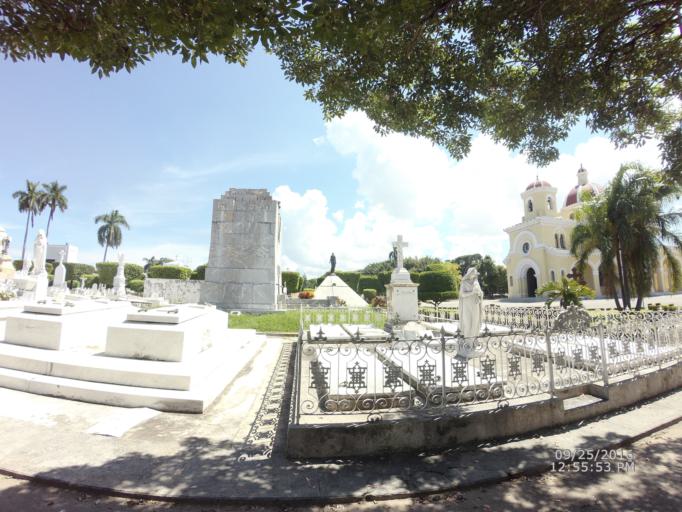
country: CU
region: La Habana
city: Havana
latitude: 23.1236
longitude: -82.3993
